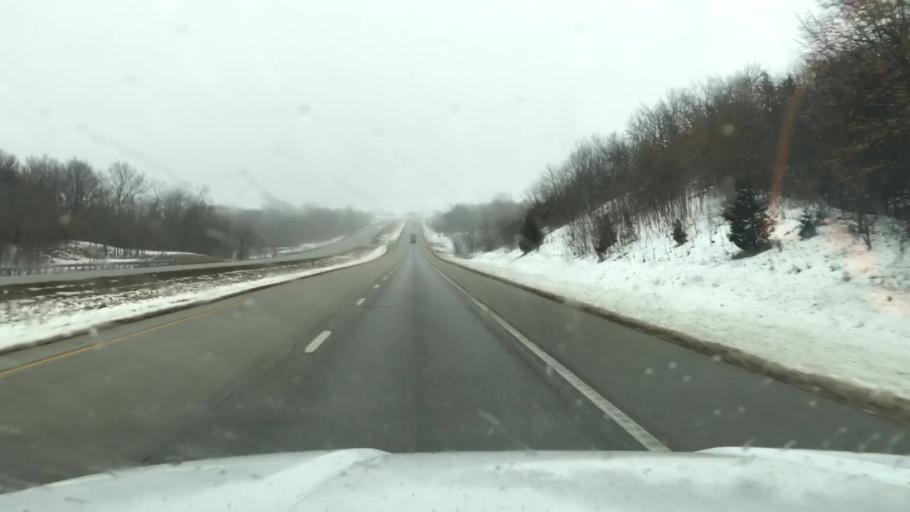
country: US
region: Missouri
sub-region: Clinton County
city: Gower
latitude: 39.7562
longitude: -94.5812
